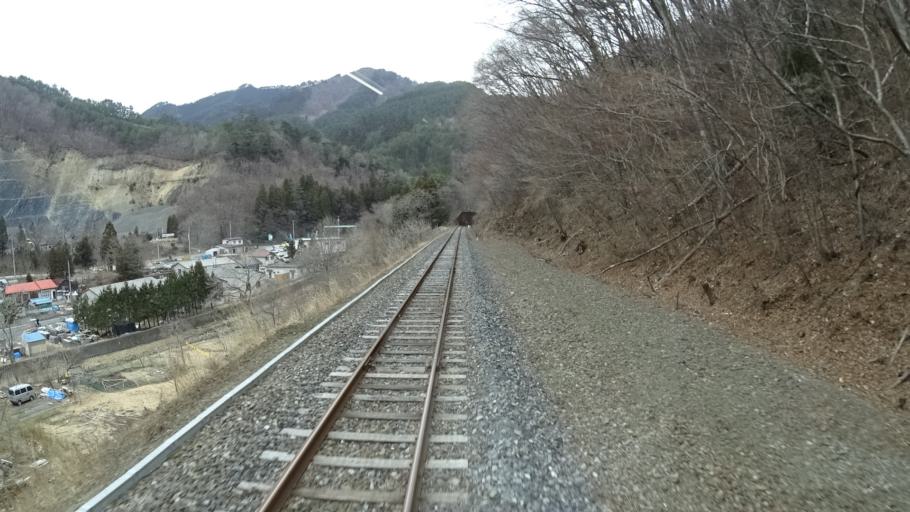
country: JP
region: Iwate
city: Kamaishi
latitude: 39.2923
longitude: 141.8631
